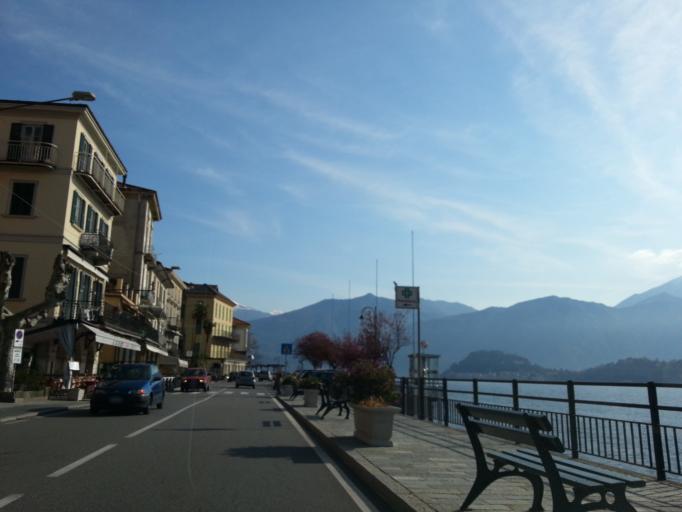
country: IT
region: Lombardy
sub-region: Provincia di Como
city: Tremezzo
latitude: 45.9832
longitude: 9.2260
